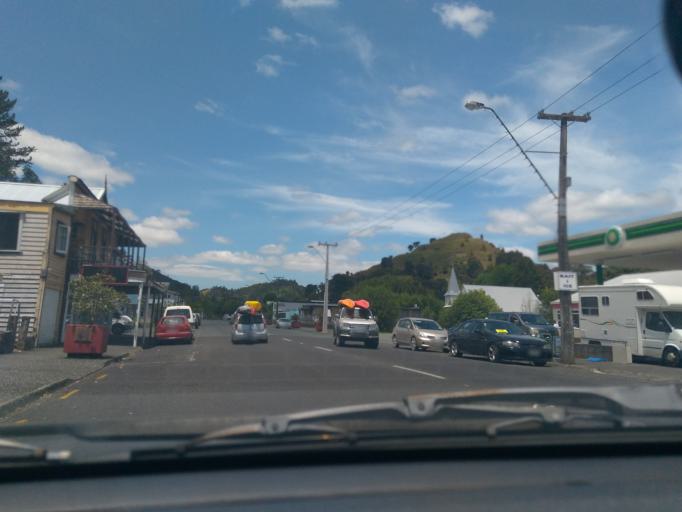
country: NZ
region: Northland
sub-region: Far North District
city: Kerikeri
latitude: -35.0999
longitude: 173.7787
